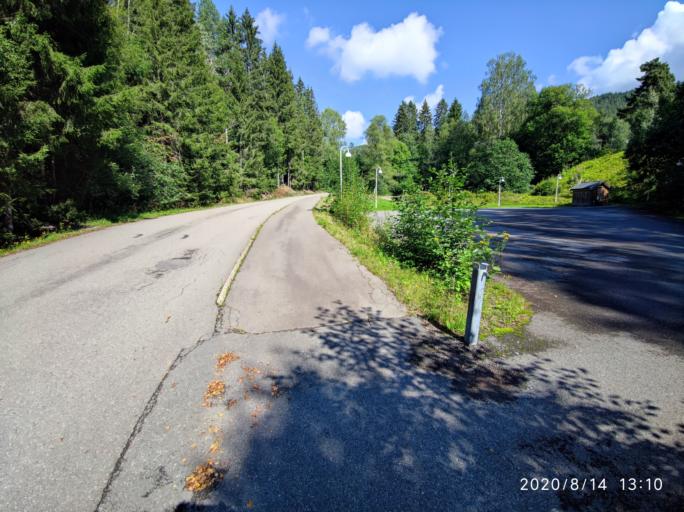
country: NO
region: Akershus
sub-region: Nittedal
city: Aneby
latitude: 60.1127
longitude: 10.8768
